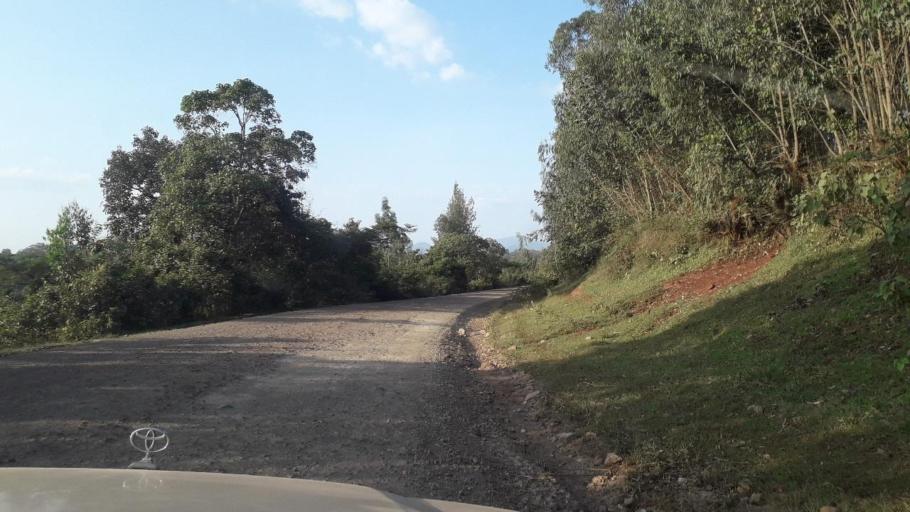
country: ET
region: Oromiya
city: Jima
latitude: 7.5760
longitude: 36.8577
